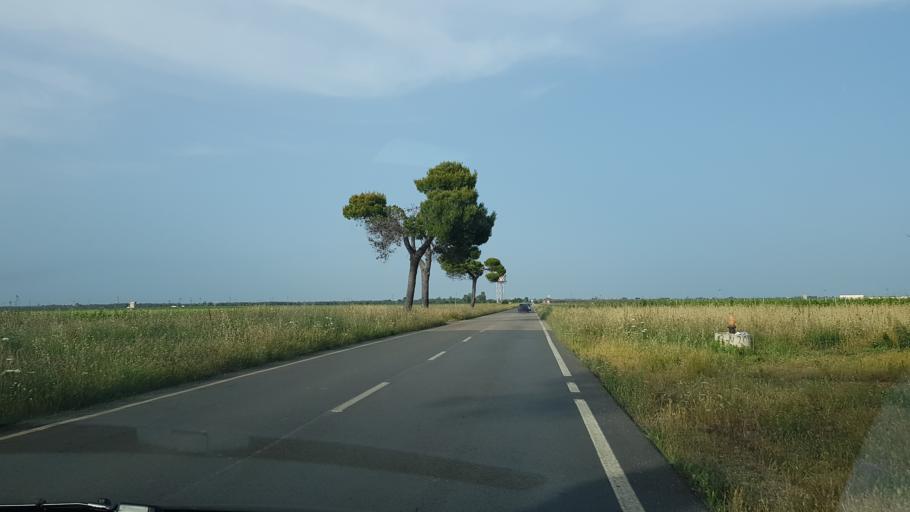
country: IT
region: Apulia
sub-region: Provincia di Brindisi
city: San Pancrazio Salentino
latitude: 40.4289
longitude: 17.8704
